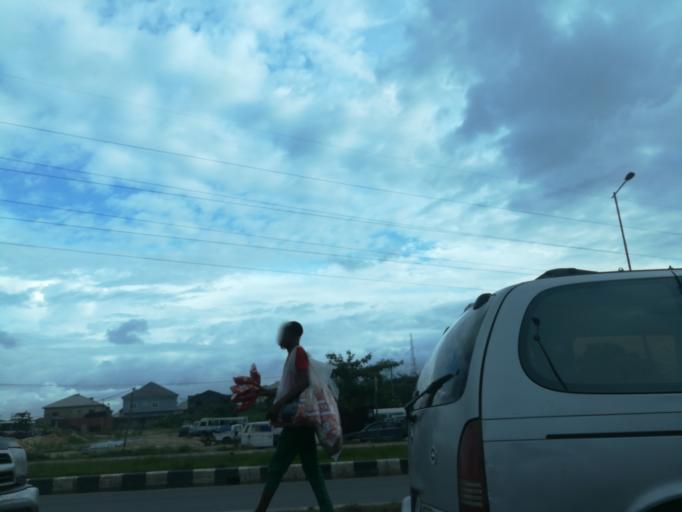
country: NG
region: Lagos
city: Ojota
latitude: 6.6123
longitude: 3.4173
